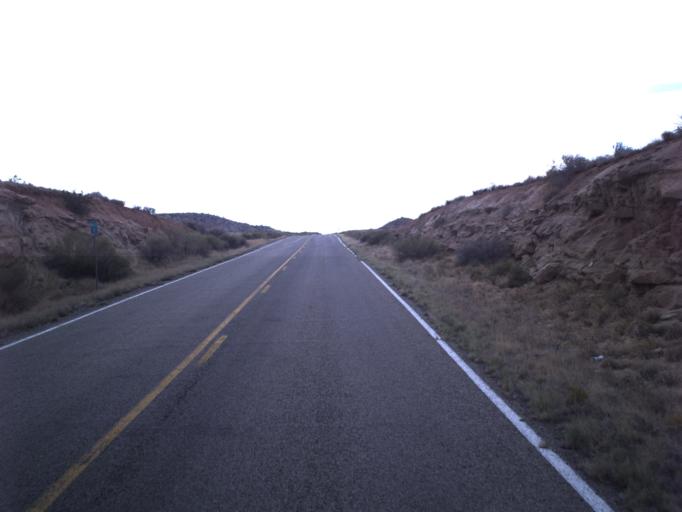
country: US
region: Utah
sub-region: San Juan County
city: Blanding
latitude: 37.4193
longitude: -109.4563
